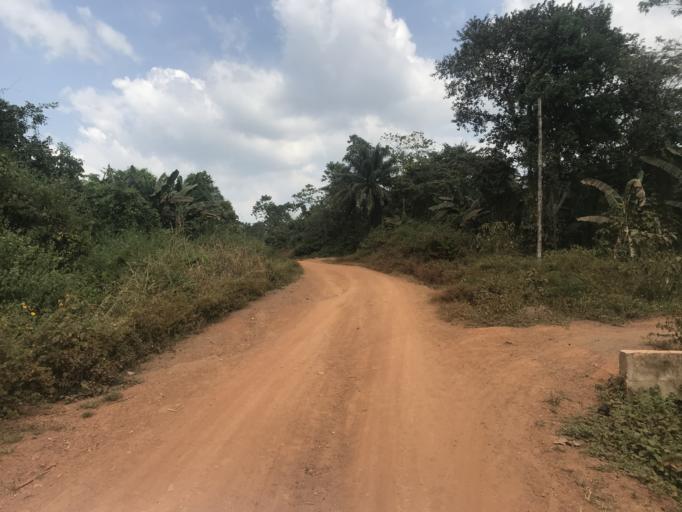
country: NG
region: Osun
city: Inisa
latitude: 7.8599
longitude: 4.3824
